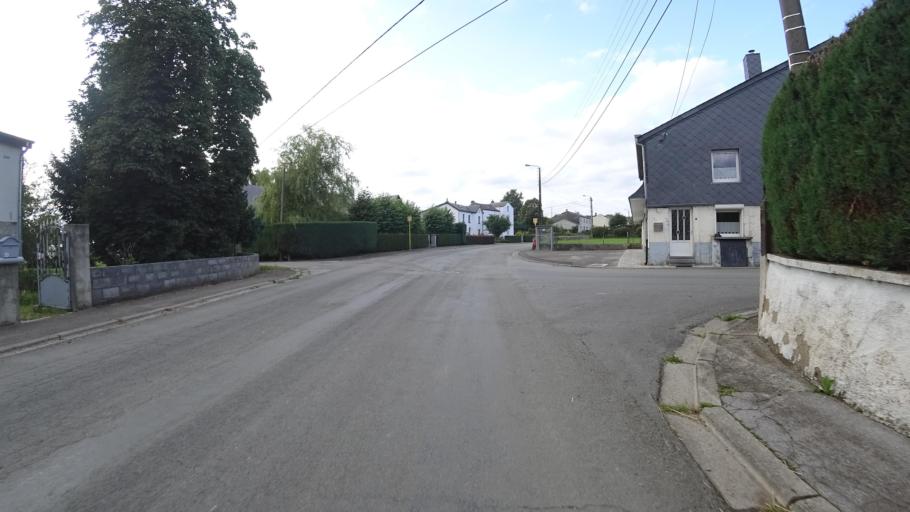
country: BE
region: Wallonia
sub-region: Province du Luxembourg
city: Bertrix
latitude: 49.8324
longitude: 5.3401
